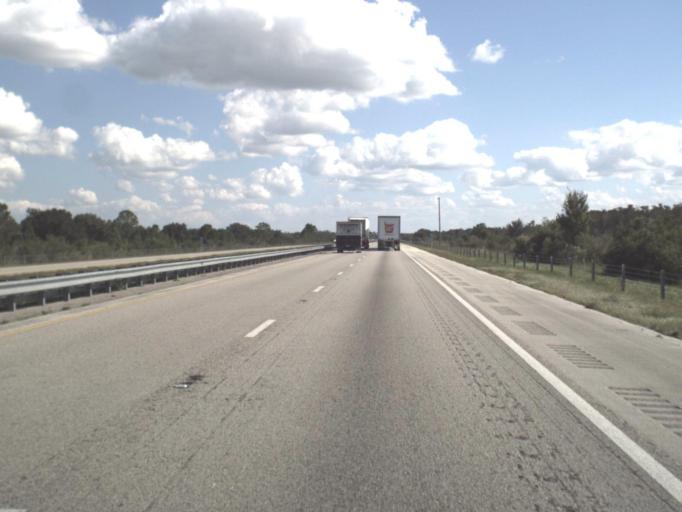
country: US
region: Florida
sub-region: Osceola County
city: Saint Cloud
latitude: 27.9423
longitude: -81.0788
